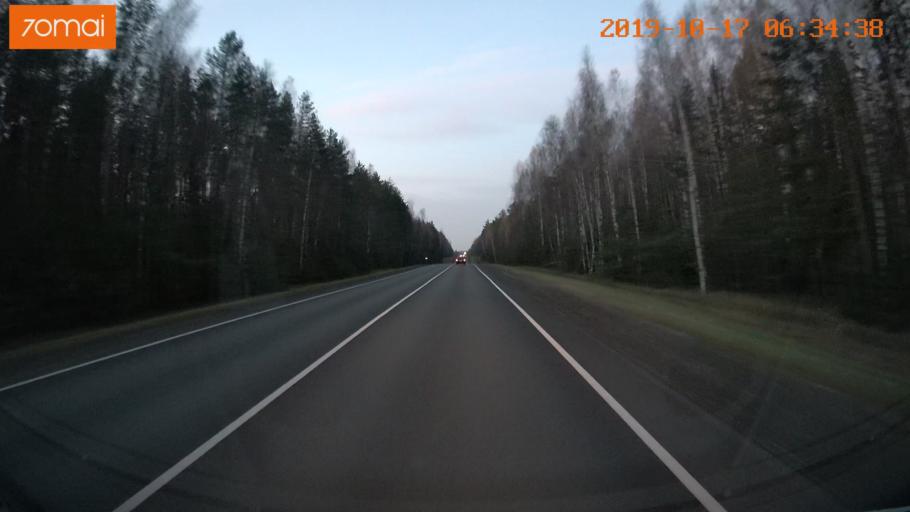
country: RU
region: Ivanovo
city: Novoye Leushino
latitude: 56.7010
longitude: 40.6351
